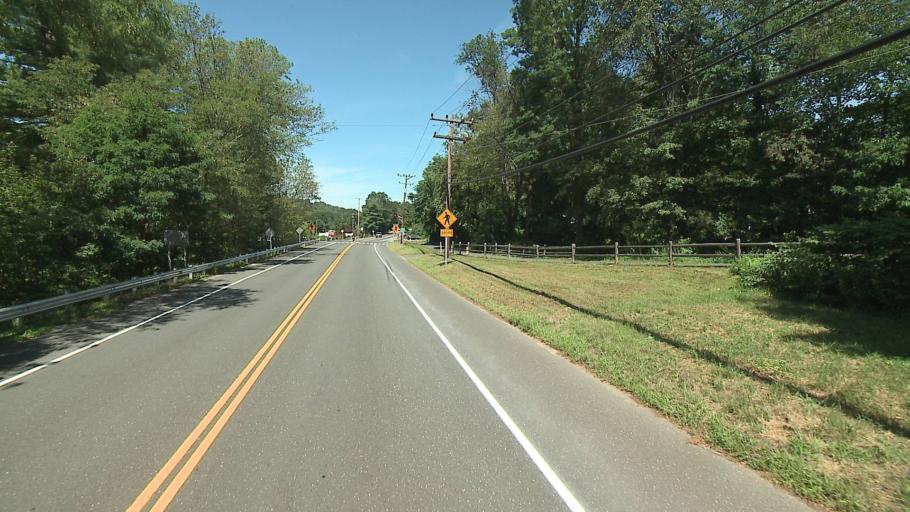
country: US
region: Connecticut
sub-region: Hartford County
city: Collinsville
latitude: 41.8194
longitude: -72.9213
